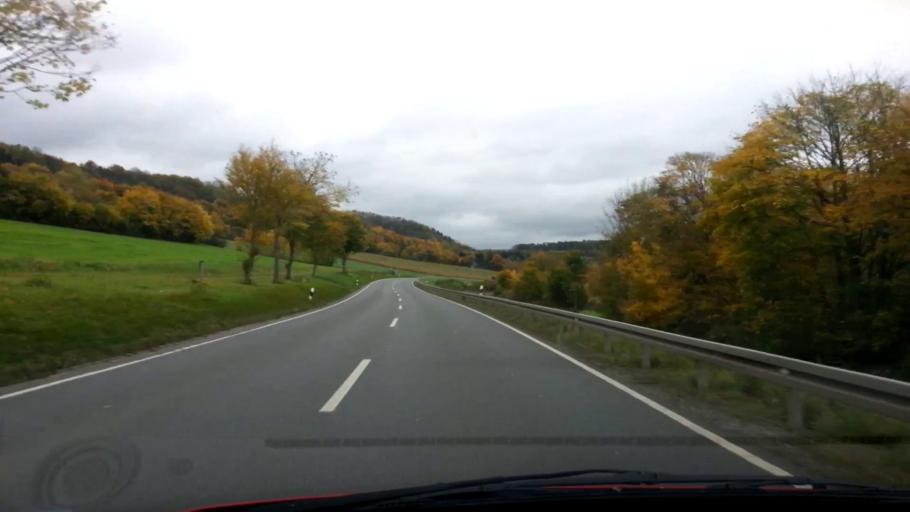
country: DE
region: Bavaria
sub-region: Upper Franconia
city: Reuth
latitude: 49.9697
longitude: 11.6660
